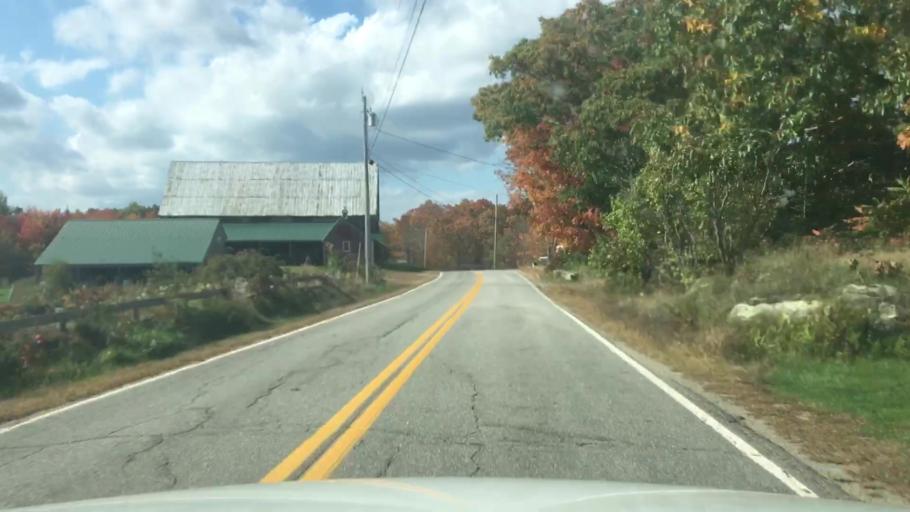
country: US
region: Maine
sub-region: Knox County
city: Washington
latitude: 44.3065
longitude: -69.3383
